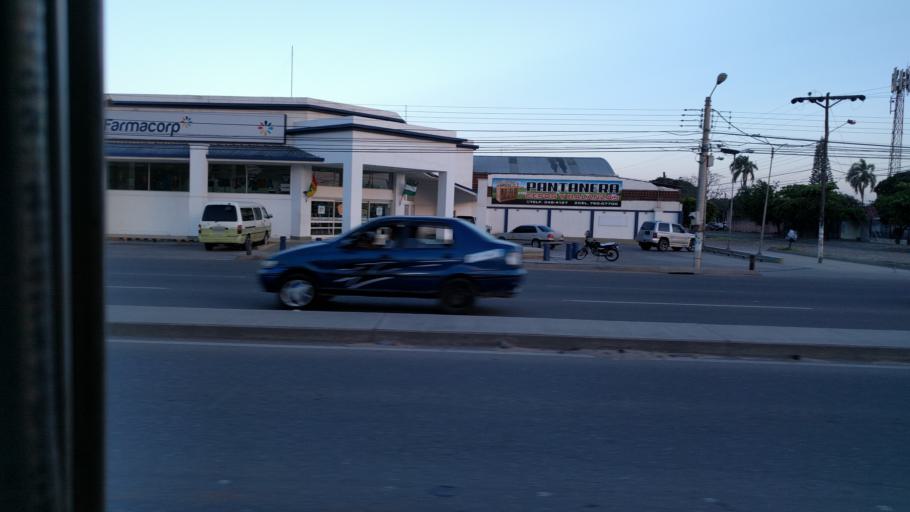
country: BO
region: Santa Cruz
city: Santa Cruz de la Sierra
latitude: -17.7750
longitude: -63.1348
